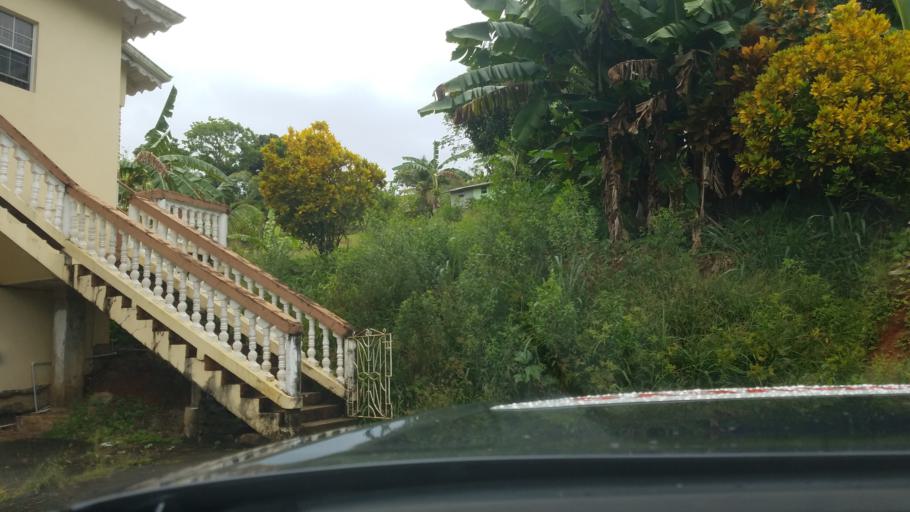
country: LC
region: Castries Quarter
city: Bisee
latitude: 14.0007
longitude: -60.9618
